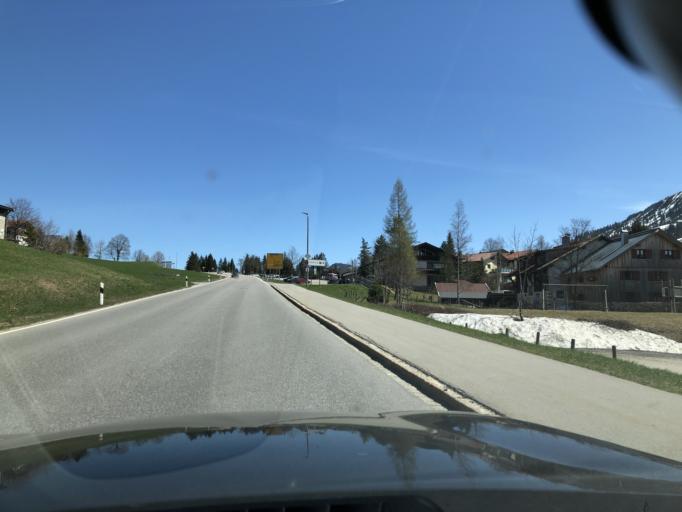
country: AT
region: Tyrol
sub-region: Politischer Bezirk Reutte
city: Schattwald
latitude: 47.5156
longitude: 10.4049
